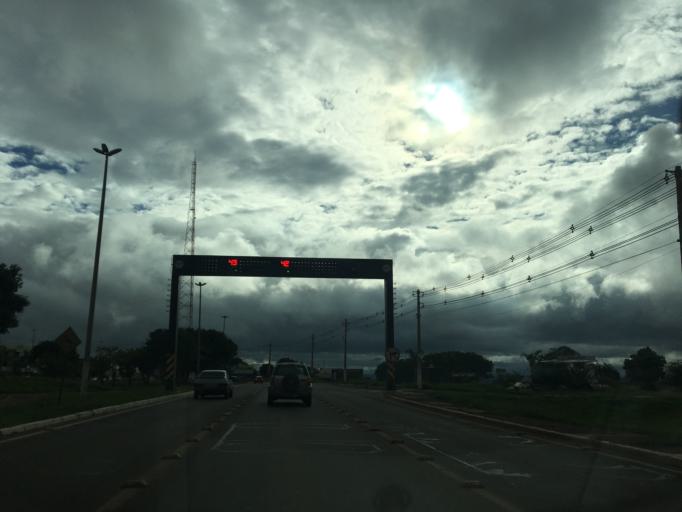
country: BR
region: Goias
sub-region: Luziania
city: Luziania
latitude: -16.0153
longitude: -48.0163
